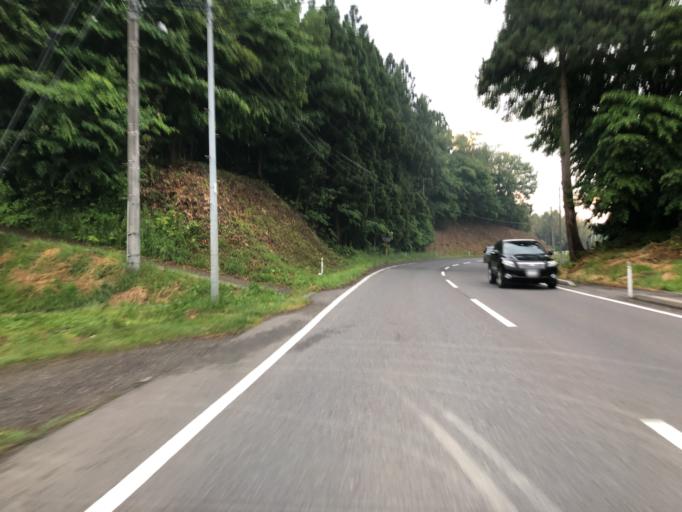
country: JP
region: Fukushima
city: Ishikawa
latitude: 37.2097
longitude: 140.4479
